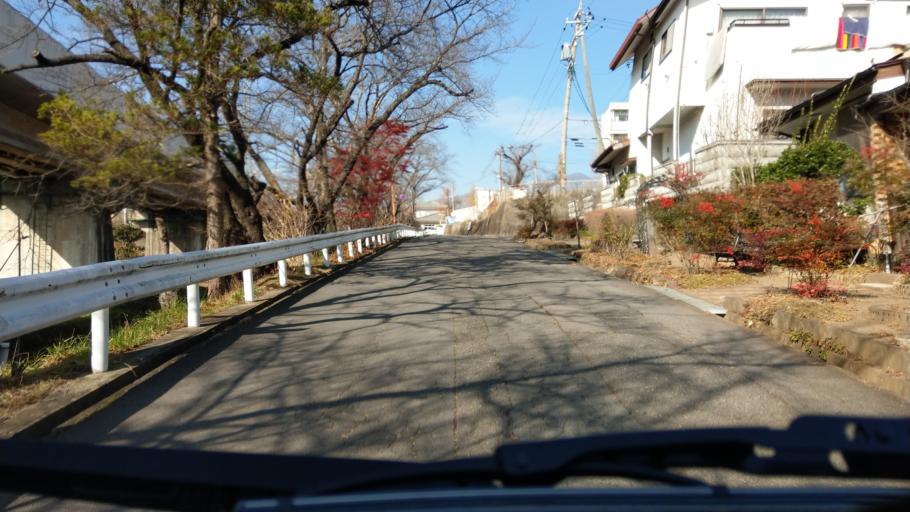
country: JP
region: Nagano
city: Komoro
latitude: 36.3315
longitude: 138.4184
